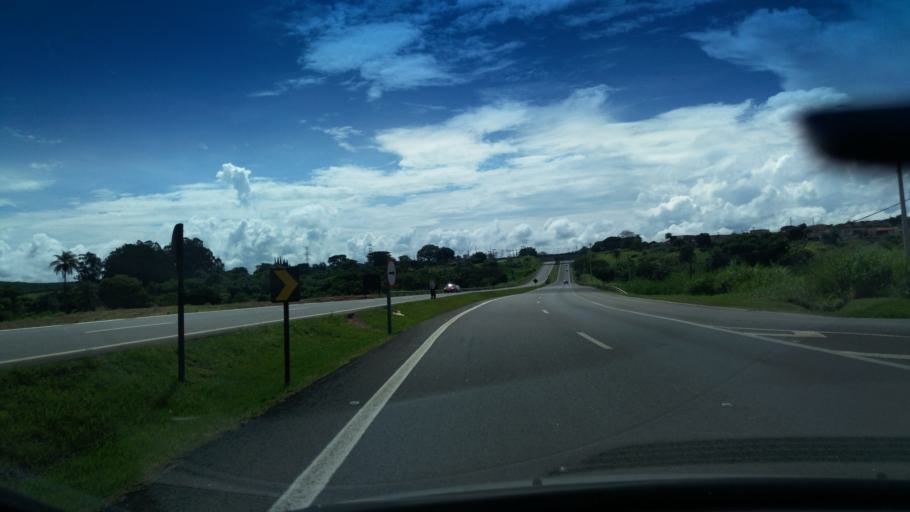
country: BR
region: Sao Paulo
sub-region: Santo Antonio Do Jardim
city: Espirito Santo do Pinhal
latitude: -22.1979
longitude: -46.7765
